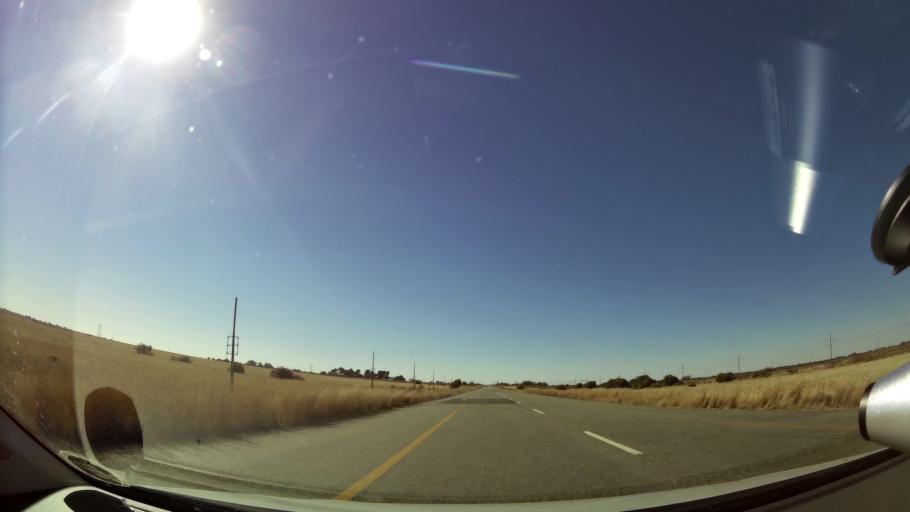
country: ZA
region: North-West
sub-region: Dr Ruth Segomotsi Mompati District Municipality
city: Bloemhof
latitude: -27.6814
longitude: 25.4569
